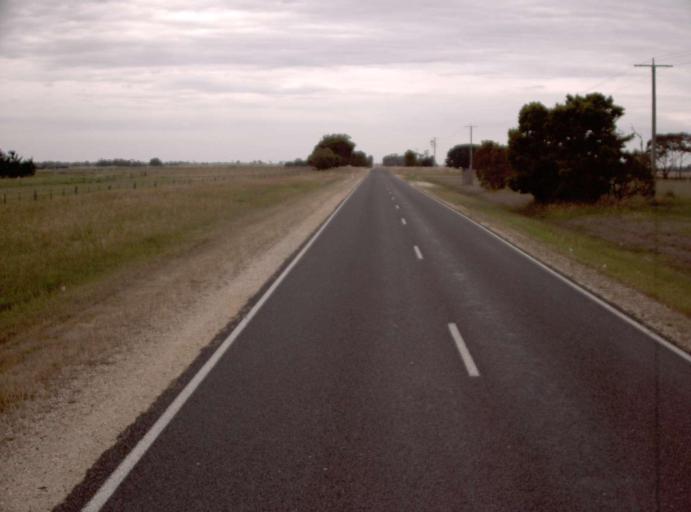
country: AU
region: Victoria
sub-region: Wellington
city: Sale
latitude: -38.1740
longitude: 147.1875
